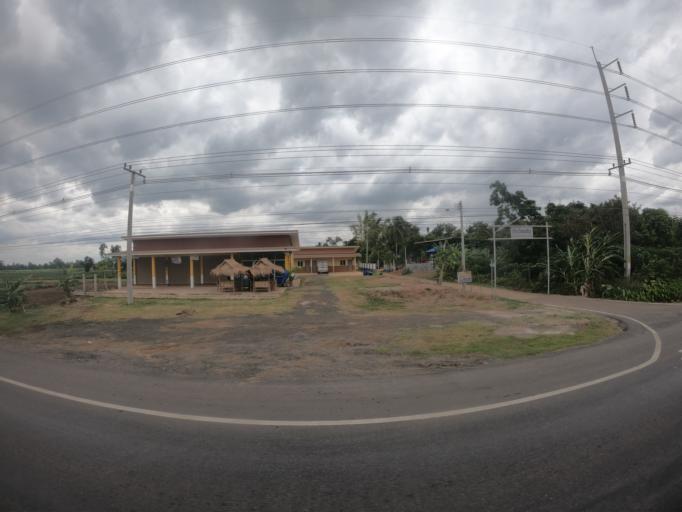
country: TH
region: Nakhon Ratchasima
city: Nong Bun Nak
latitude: 14.7142
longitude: 102.4508
